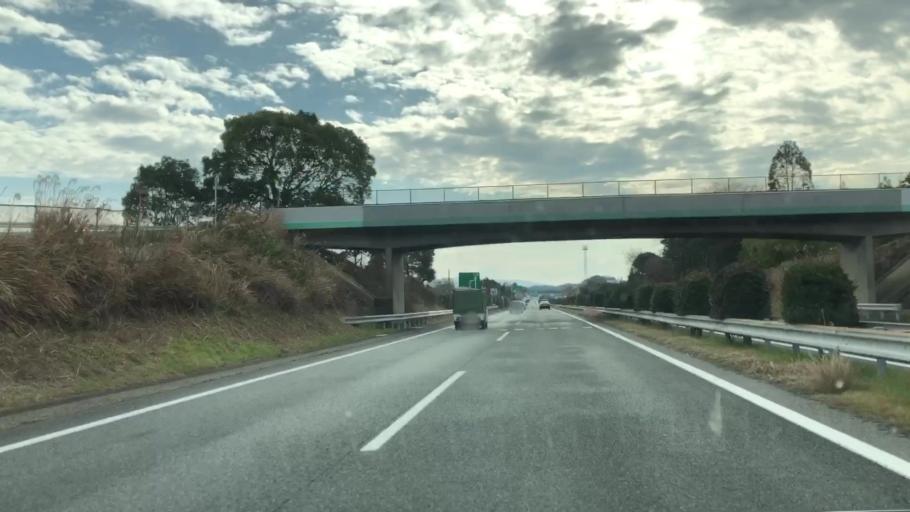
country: JP
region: Fukuoka
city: Kurume
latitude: 33.2648
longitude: 130.5388
